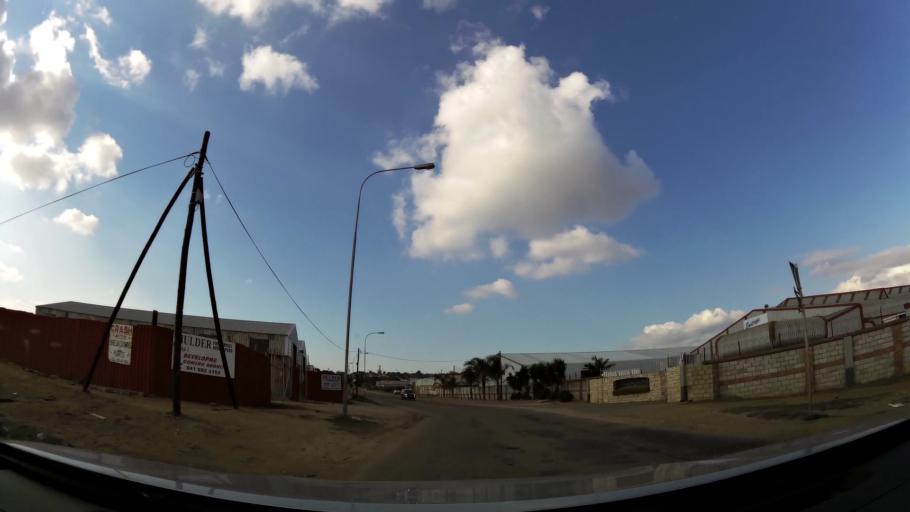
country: ZA
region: Eastern Cape
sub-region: Nelson Mandela Bay Metropolitan Municipality
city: Uitenhage
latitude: -33.7741
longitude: 25.3913
